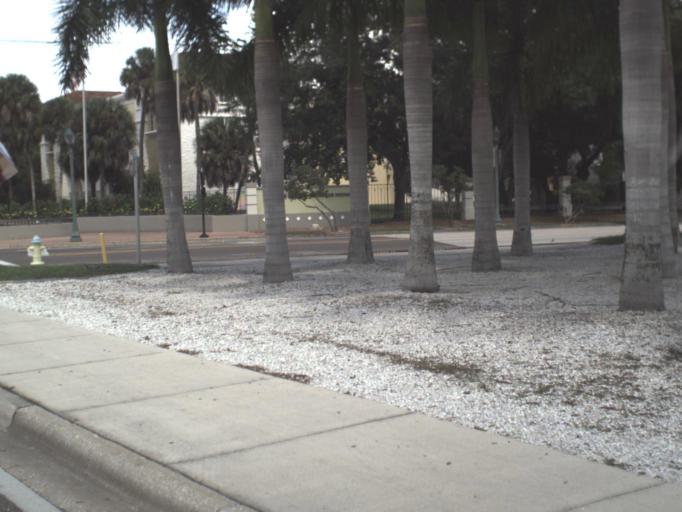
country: US
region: Florida
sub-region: Sarasota County
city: Sarasota
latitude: 27.3596
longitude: -82.5489
